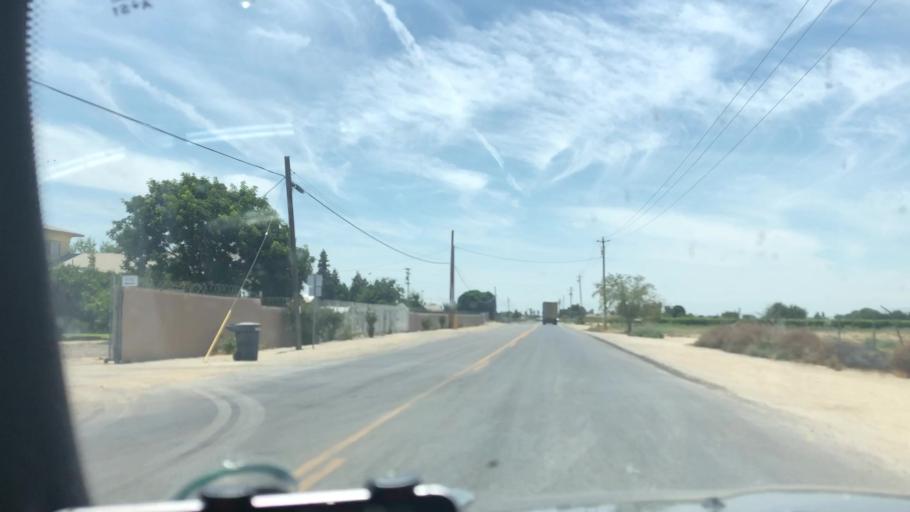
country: US
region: California
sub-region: Fresno County
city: Easton
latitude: 36.6776
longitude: -119.7547
